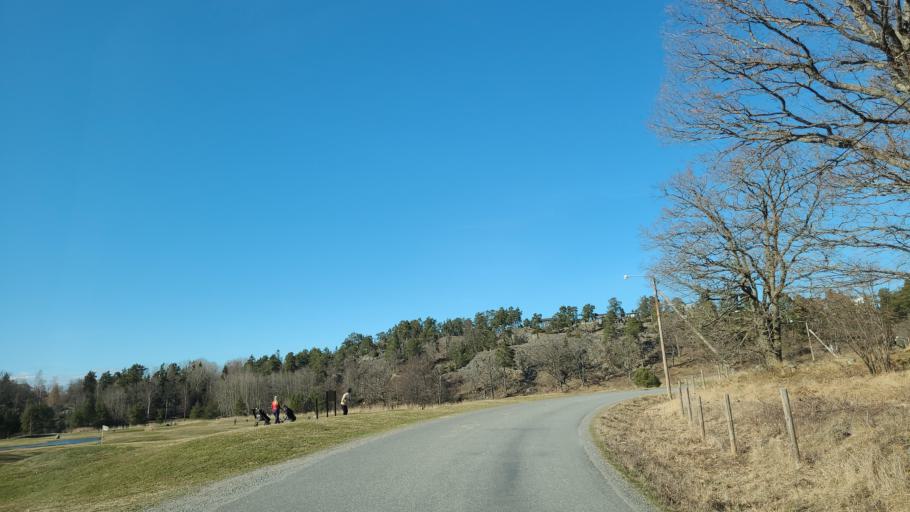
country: SE
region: Stockholm
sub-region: Varmdo Kommun
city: Hemmesta
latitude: 59.2756
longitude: 18.5475
